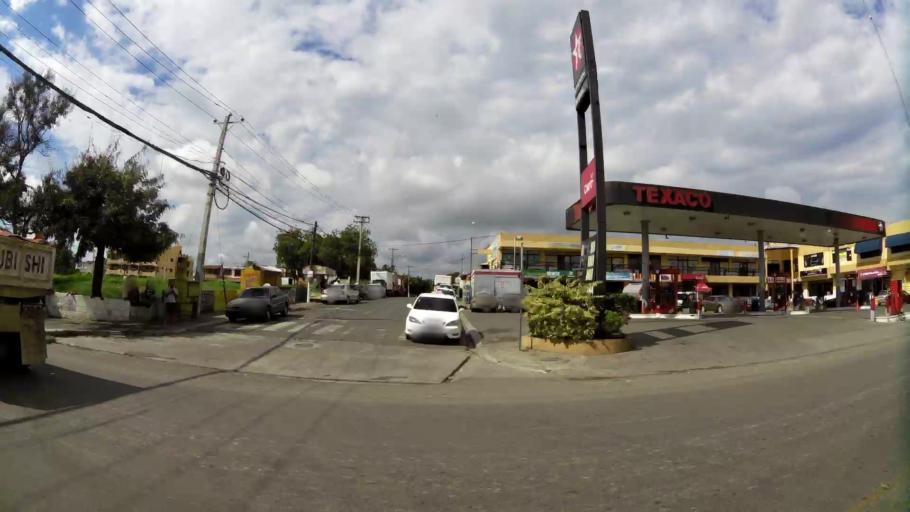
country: DO
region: Santiago
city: Santiago de los Caballeros
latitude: 19.4762
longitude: -70.7233
